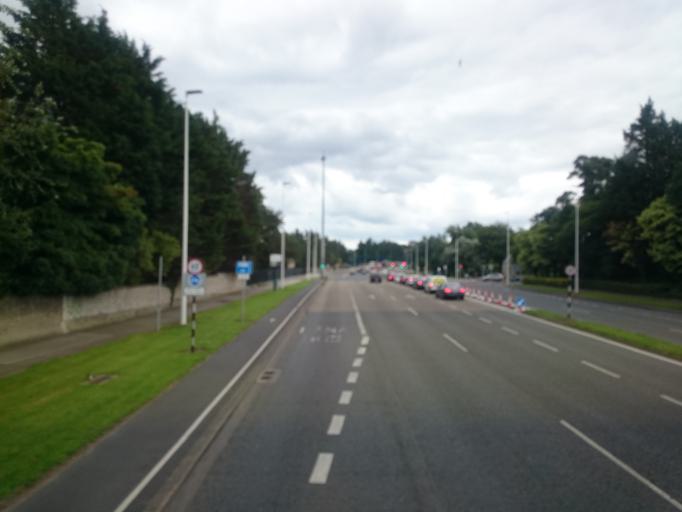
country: IE
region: Leinster
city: Mount Merrion
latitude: 53.3044
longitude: -6.2095
